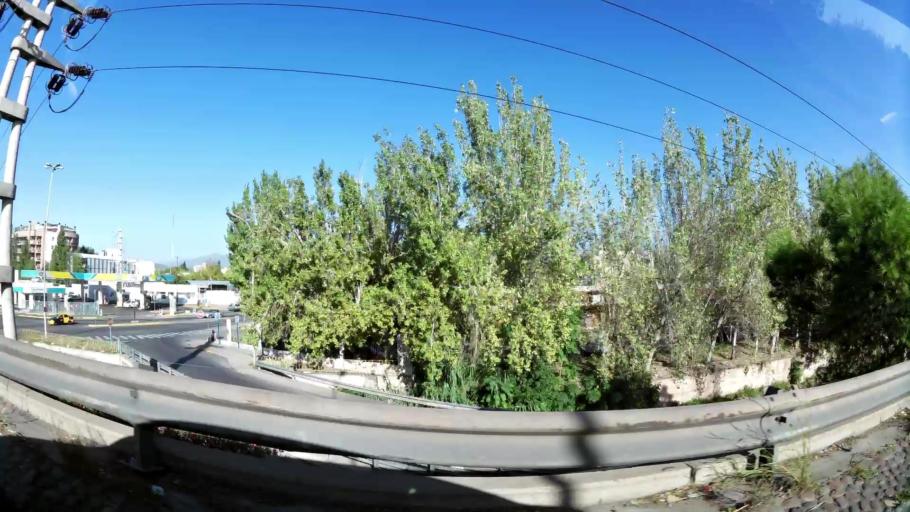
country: AR
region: Mendoza
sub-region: Departamento de Godoy Cruz
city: Godoy Cruz
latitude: -32.9087
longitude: -68.8378
